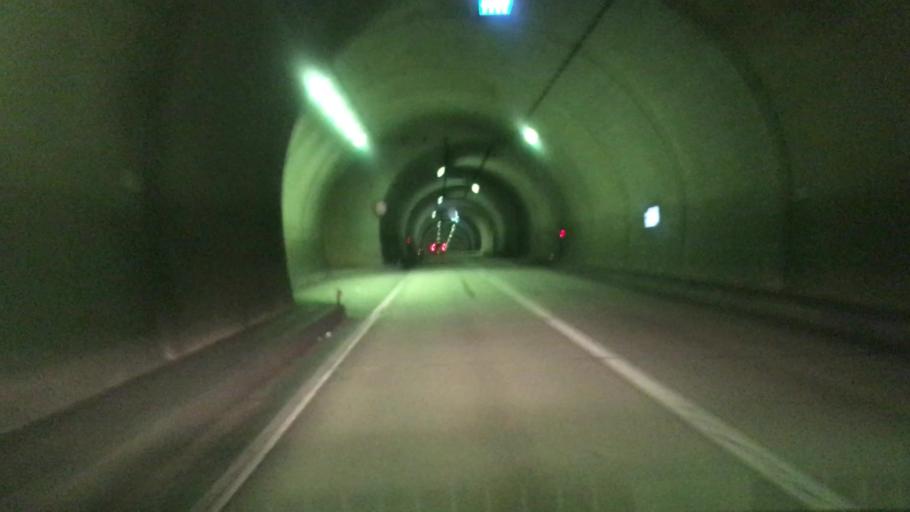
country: JP
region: Hyogo
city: Toyooka
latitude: 35.4179
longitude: 134.7402
